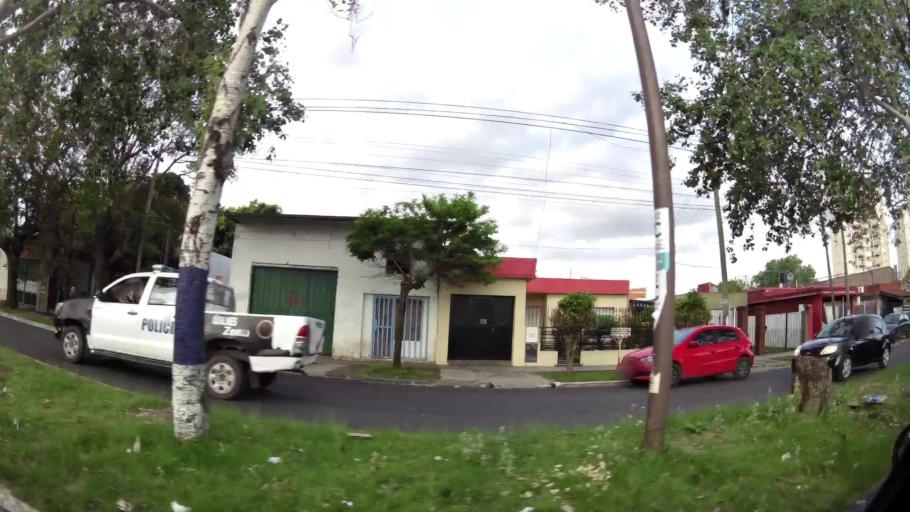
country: AR
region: Buenos Aires
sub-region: Partido de Quilmes
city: Quilmes
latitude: -34.7415
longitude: -58.2513
